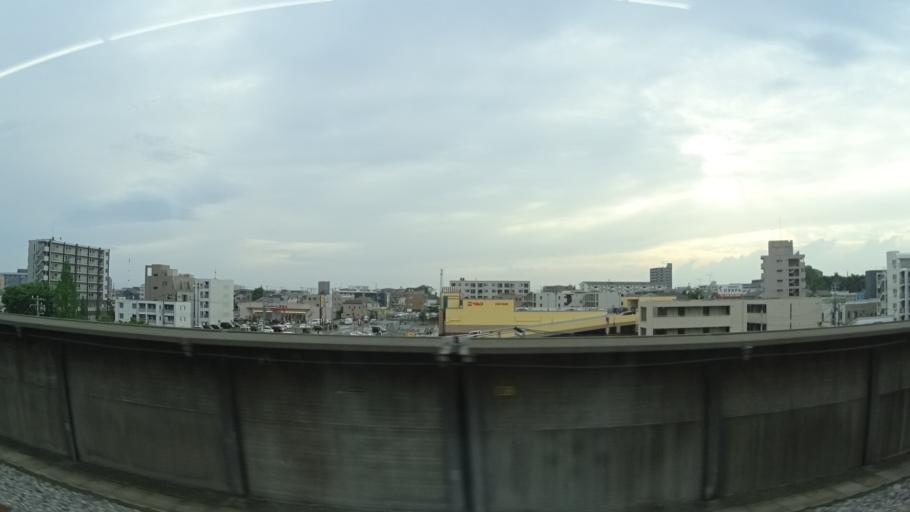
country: JP
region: Saitama
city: Yono
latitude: 35.8698
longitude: 139.6301
